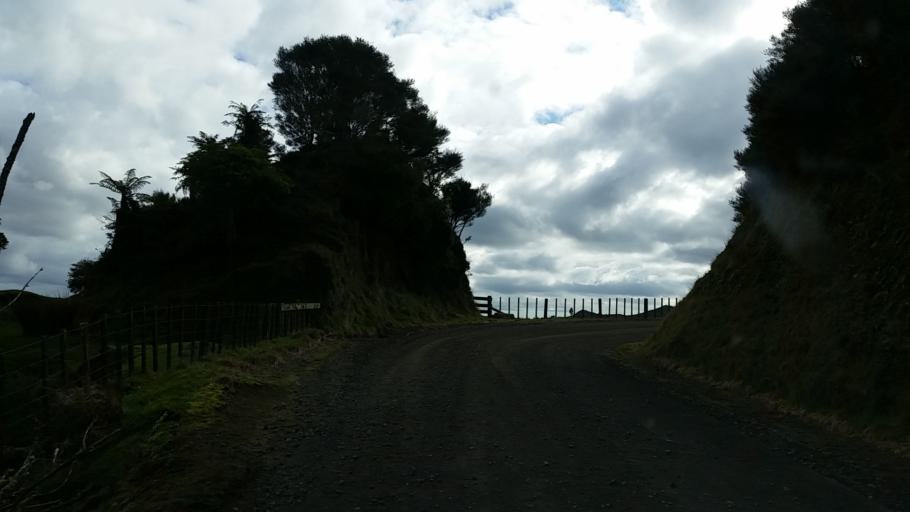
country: NZ
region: Taranaki
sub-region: South Taranaki District
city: Eltham
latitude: -39.1722
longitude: 174.6186
